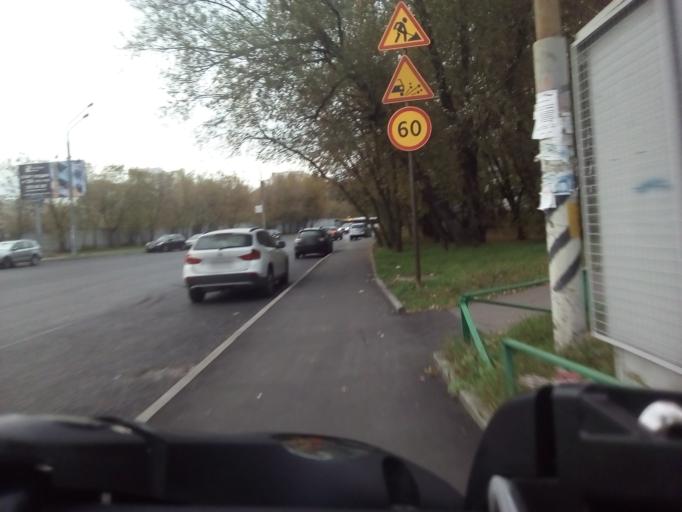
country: RU
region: Moscow
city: Sviblovo
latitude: 55.8468
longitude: 37.6402
